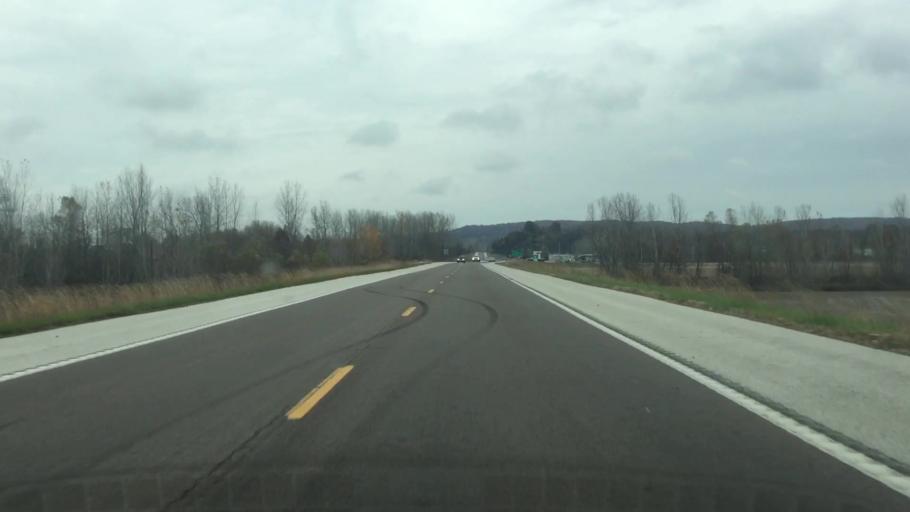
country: US
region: Missouri
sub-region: Gasconade County
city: Hermann
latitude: 38.7244
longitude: -91.4446
